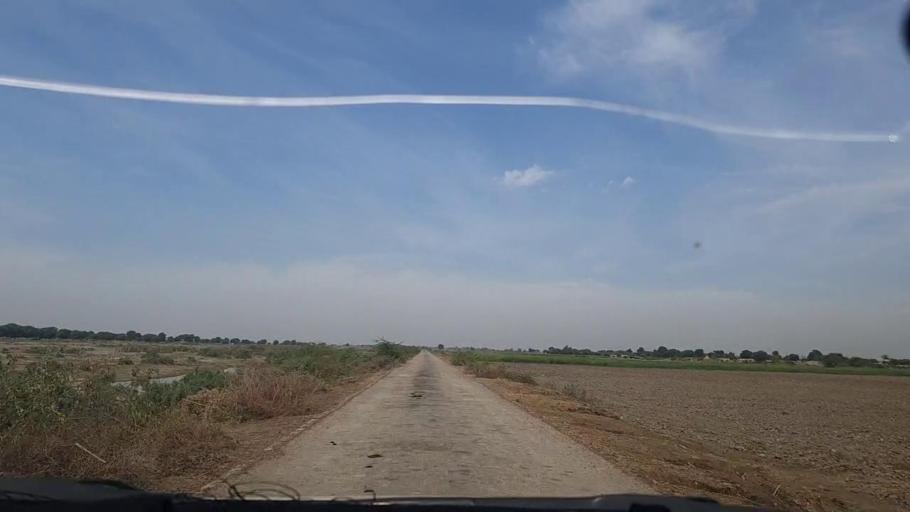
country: PK
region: Sindh
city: Pithoro
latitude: 25.4650
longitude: 69.4701
